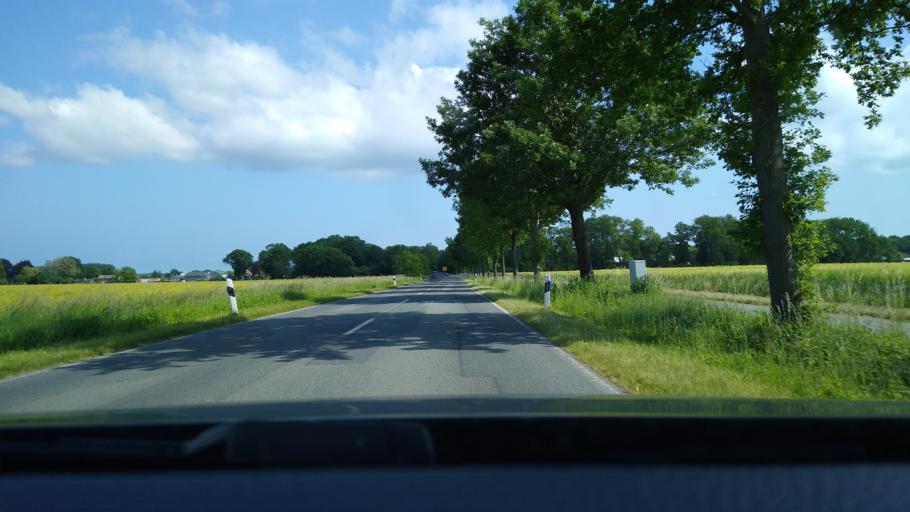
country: DE
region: Schleswig-Holstein
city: Riepsdorf
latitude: 54.1951
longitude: 10.9800
